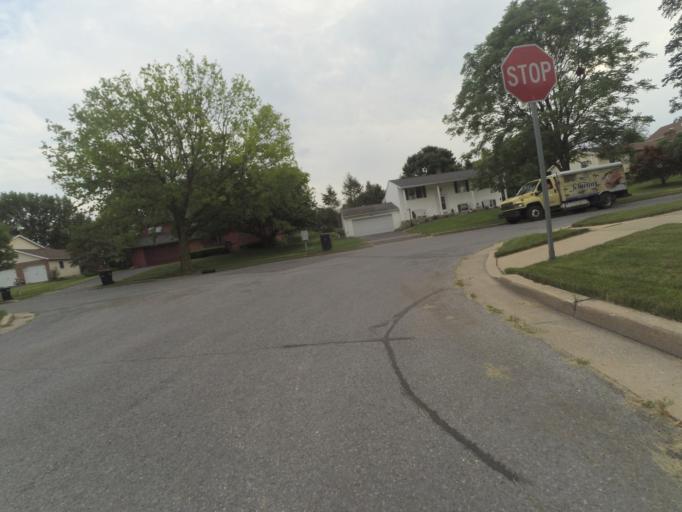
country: US
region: Pennsylvania
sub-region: Centre County
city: State College
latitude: 40.7796
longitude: -77.8671
